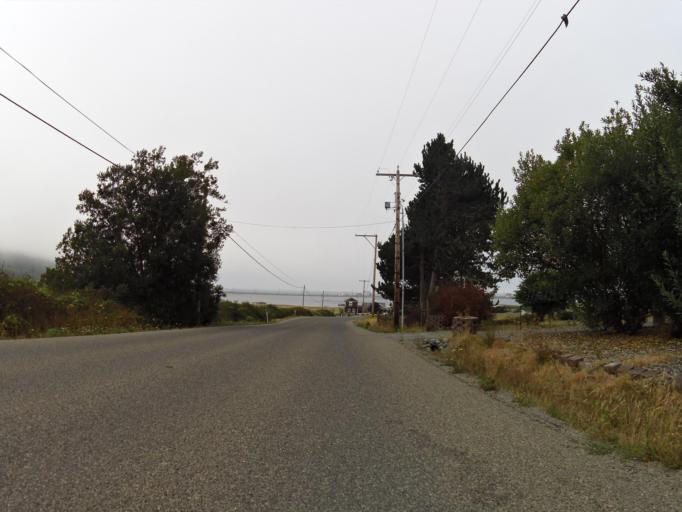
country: US
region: Washington
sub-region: Island County
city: Ault Field
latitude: 48.3006
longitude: -122.7104
